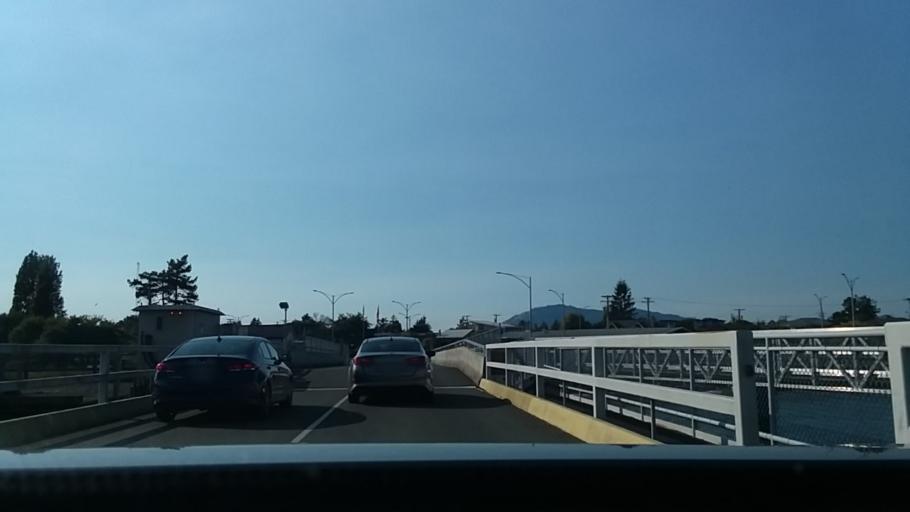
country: CA
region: British Columbia
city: North Saanich
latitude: 48.6432
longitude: -123.3966
